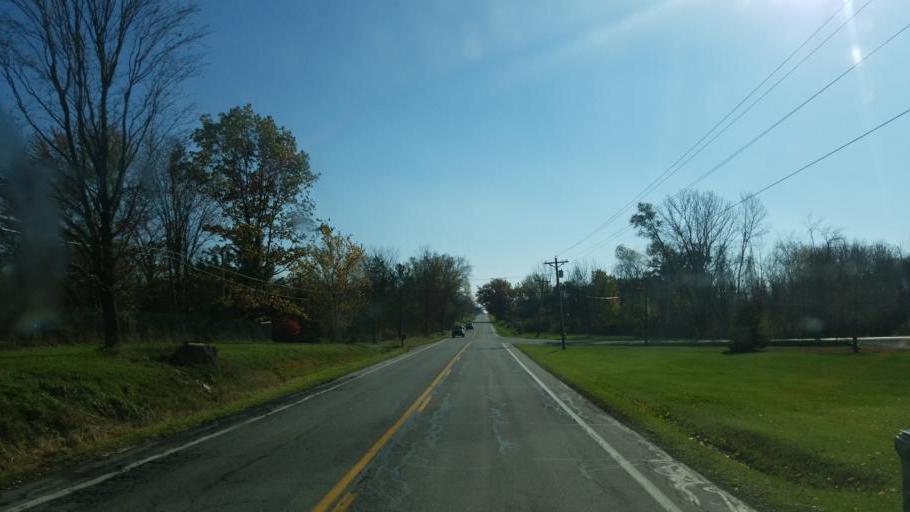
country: US
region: Ohio
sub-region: Lorain County
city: Wellington
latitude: 41.1155
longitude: -82.2198
